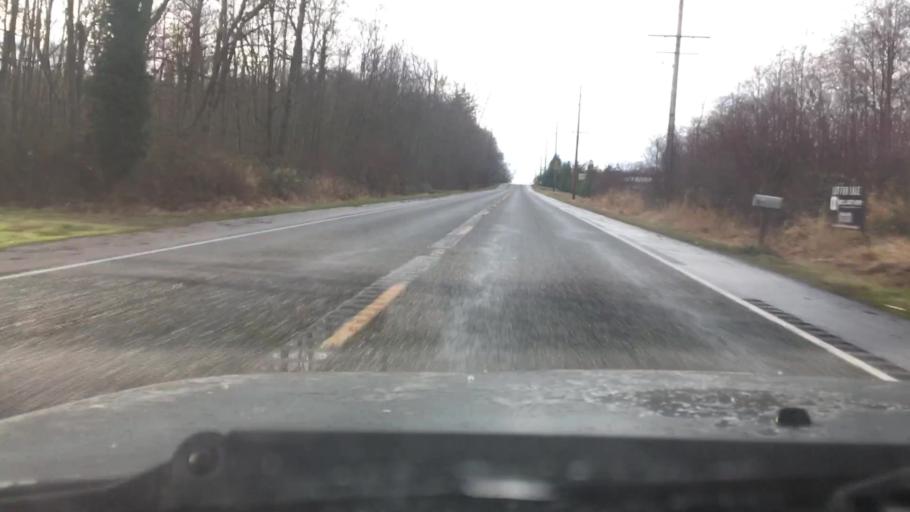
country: US
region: Washington
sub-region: Whatcom County
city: Ferndale
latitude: 48.8195
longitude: -122.6756
